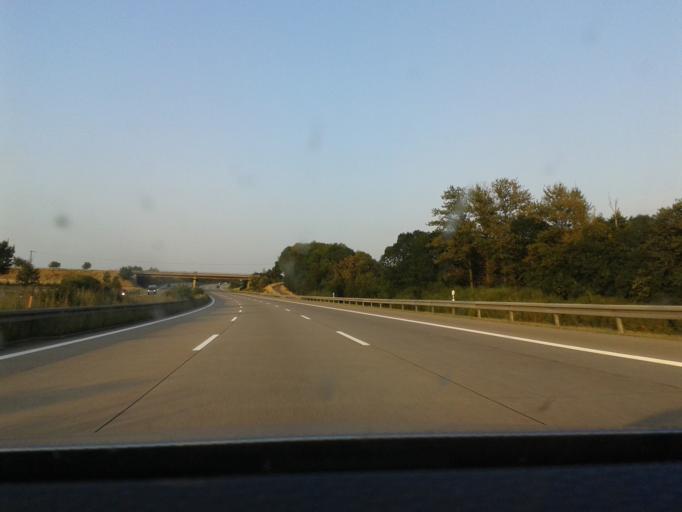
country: DE
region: Saxony
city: Niederschona
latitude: 51.0580
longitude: 13.4411
